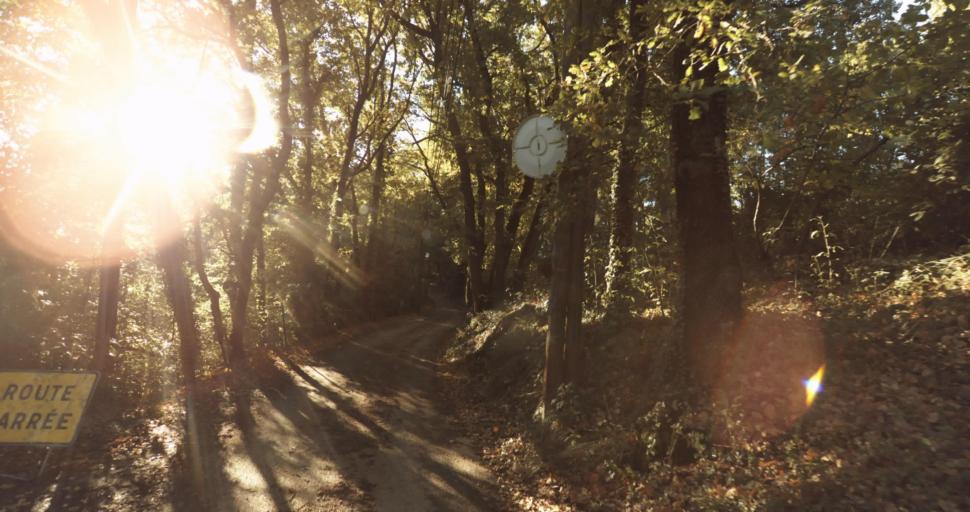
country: FR
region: Provence-Alpes-Cote d'Azur
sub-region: Departement des Bouches-du-Rhone
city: Venelles
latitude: 43.6083
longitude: 5.4809
